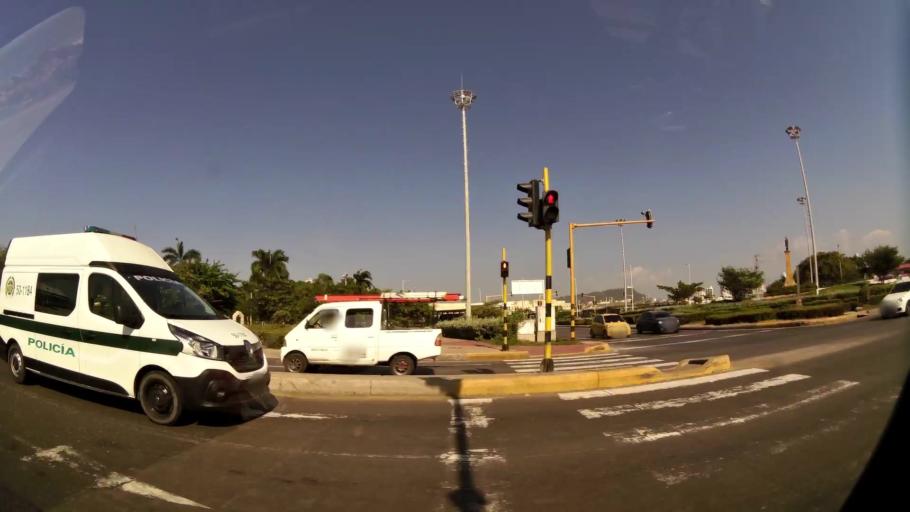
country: CO
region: Bolivar
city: Cartagena
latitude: 10.4193
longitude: -75.5527
